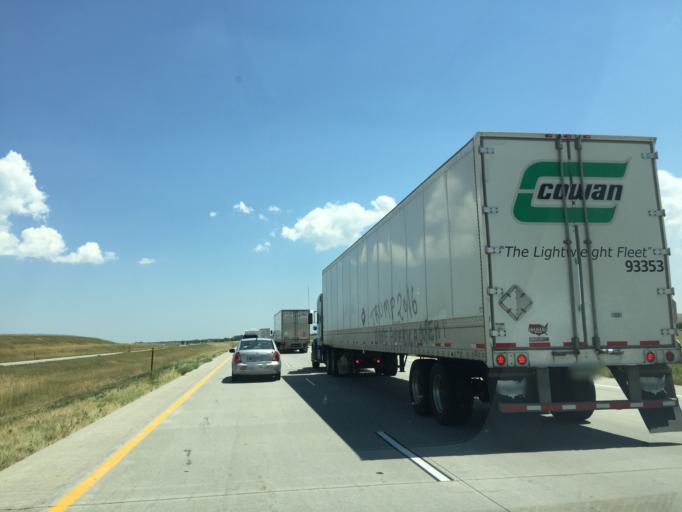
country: US
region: Colorado
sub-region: Lincoln County
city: Limon
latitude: 39.2888
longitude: -103.7912
